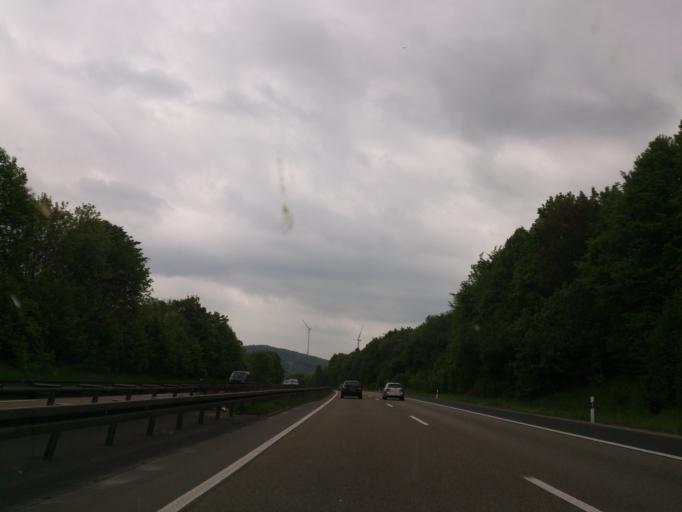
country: DE
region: Hesse
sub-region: Regierungsbezirk Kassel
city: Martinhagen
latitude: 51.3164
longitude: 9.2884
